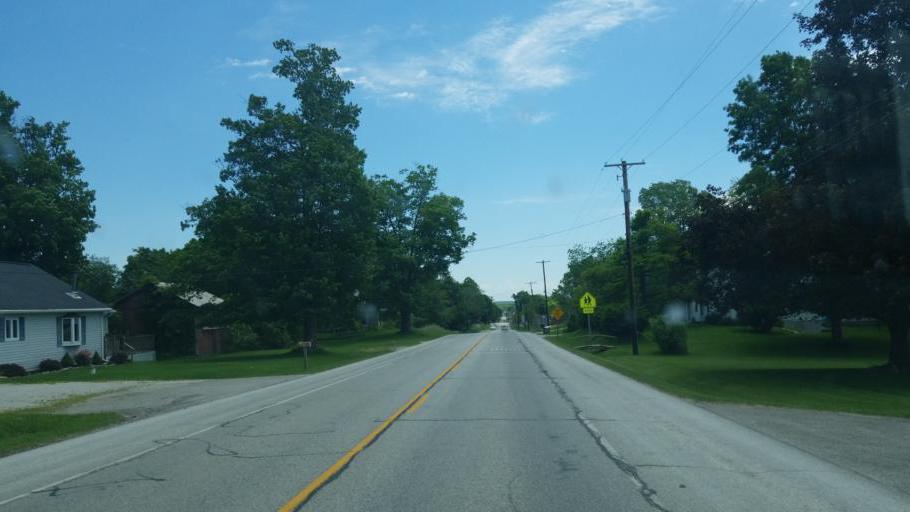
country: US
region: Ohio
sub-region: Geauga County
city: Middlefield
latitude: 41.4584
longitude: -80.9632
